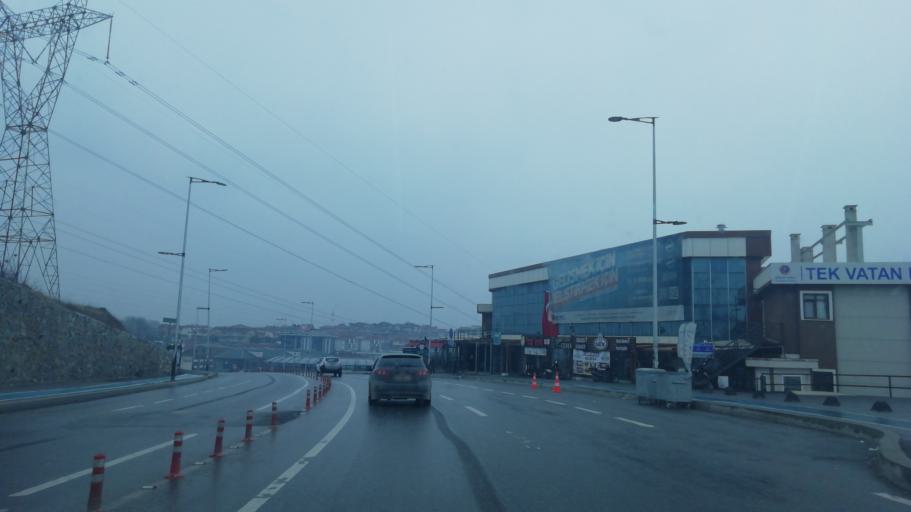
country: TR
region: Sakarya
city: Adapazari
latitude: 40.7468
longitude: 30.3505
